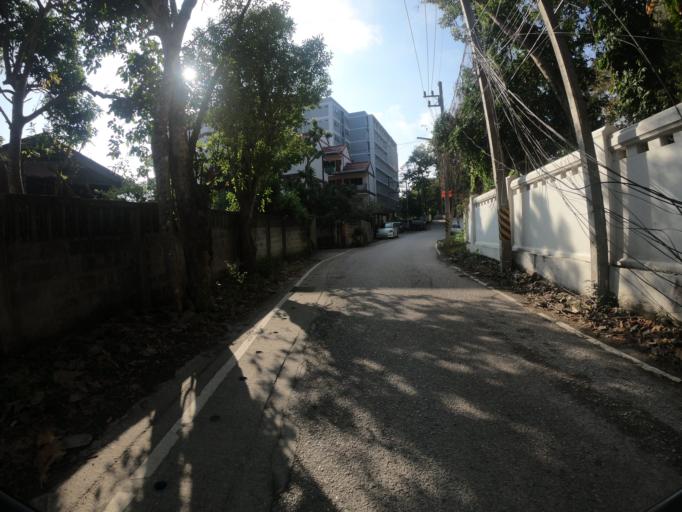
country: TH
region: Chiang Mai
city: Chiang Mai
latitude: 18.8136
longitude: 98.9550
